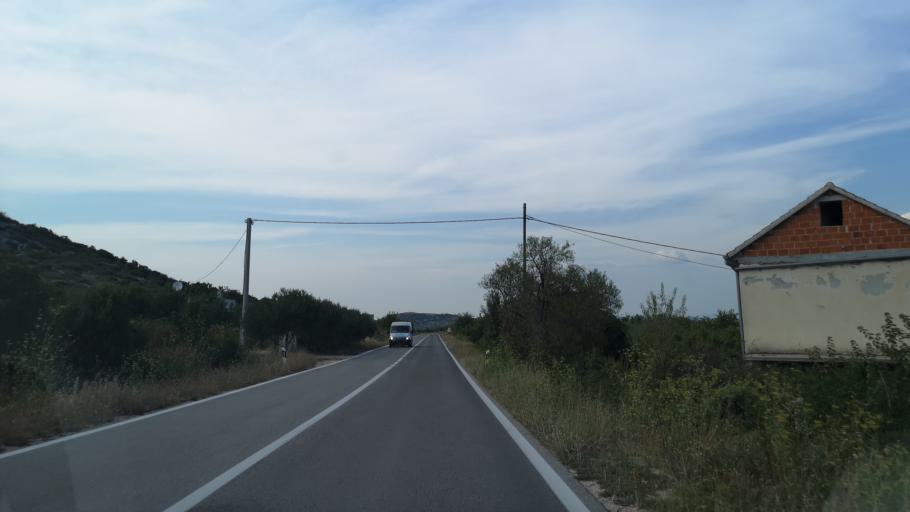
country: HR
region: Sibensko-Kniniska
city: Zaton
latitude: 43.8361
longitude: 15.7776
